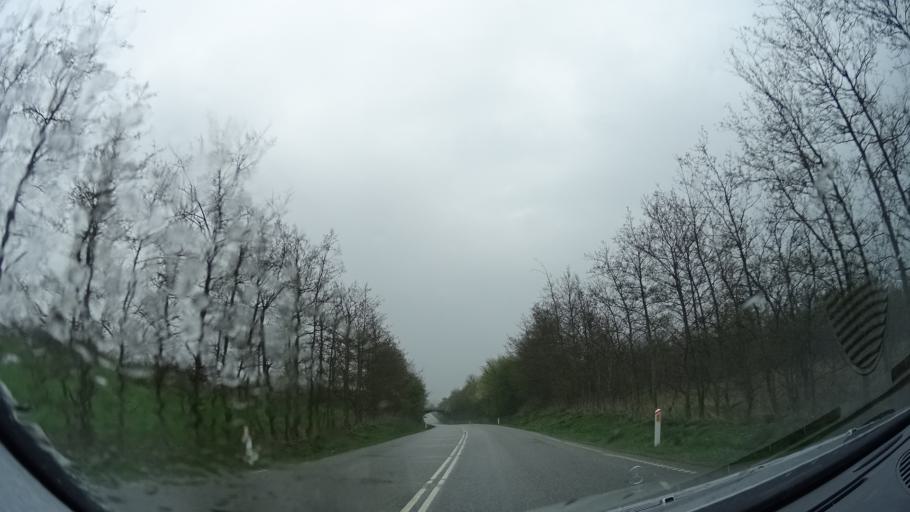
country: DK
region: Zealand
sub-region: Odsherred Kommune
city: Hojby
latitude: 55.8444
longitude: 11.5724
